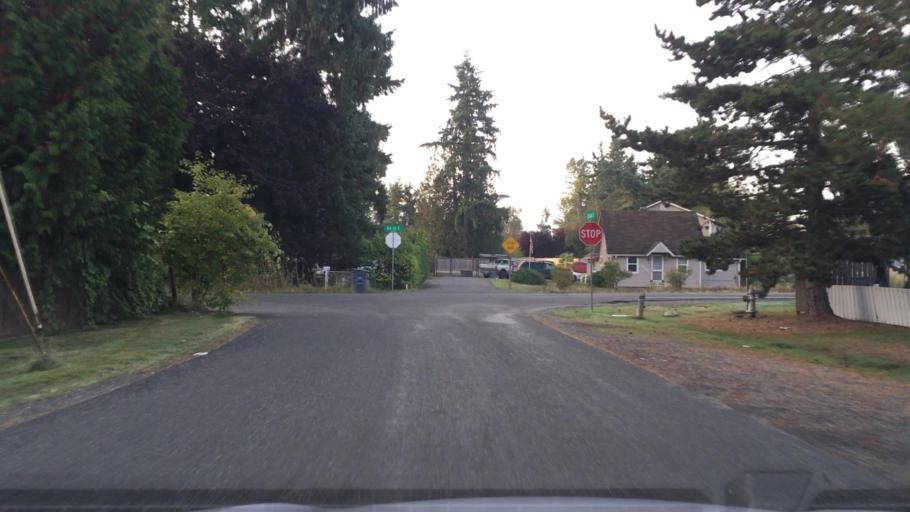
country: US
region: Washington
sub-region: Pierce County
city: Midland
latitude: 47.1807
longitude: -122.4024
